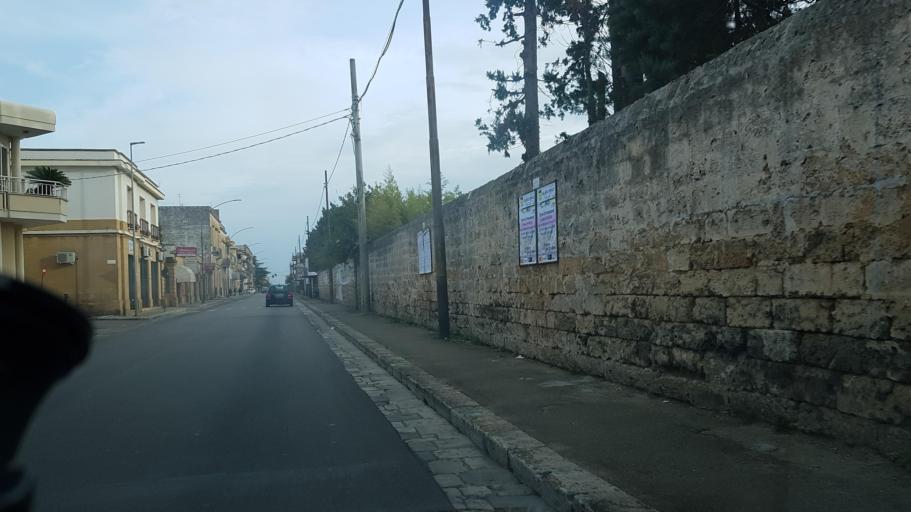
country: IT
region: Apulia
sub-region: Provincia di Lecce
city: Trepuzzi
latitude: 40.4039
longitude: 18.0727
